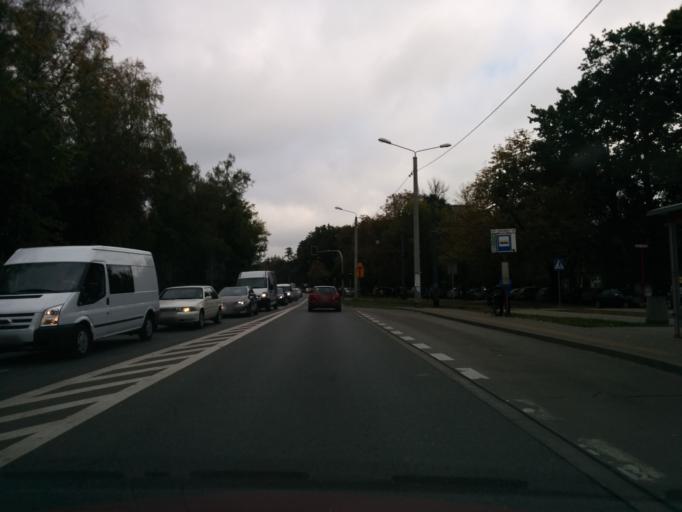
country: PL
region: Masovian Voivodeship
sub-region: Warszawa
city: Bemowo
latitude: 52.2496
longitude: 20.8982
